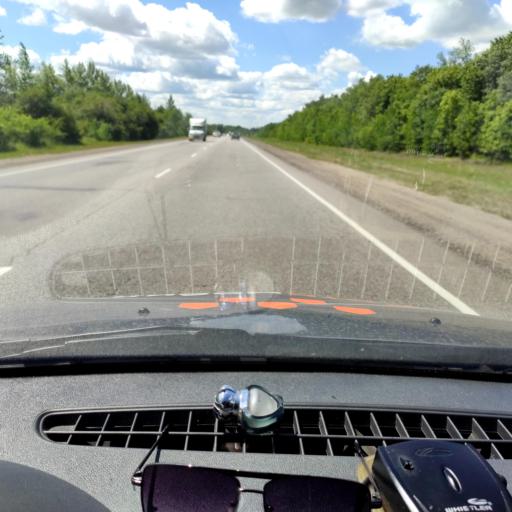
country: RU
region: Lipetsk
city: Borinskoye
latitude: 52.4307
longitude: 39.2666
